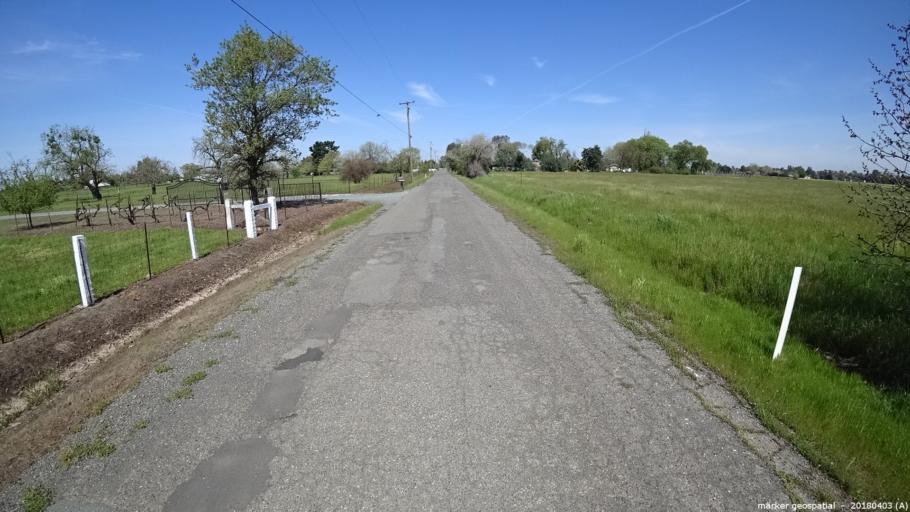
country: US
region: California
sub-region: Sacramento County
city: Wilton
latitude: 38.3974
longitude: -121.2691
